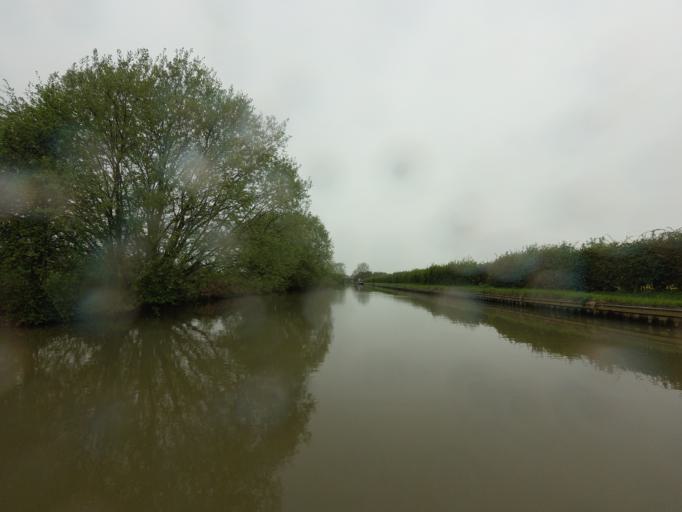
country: GB
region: England
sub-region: Milton Keynes
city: Castlethorpe
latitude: 52.0978
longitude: -0.8740
